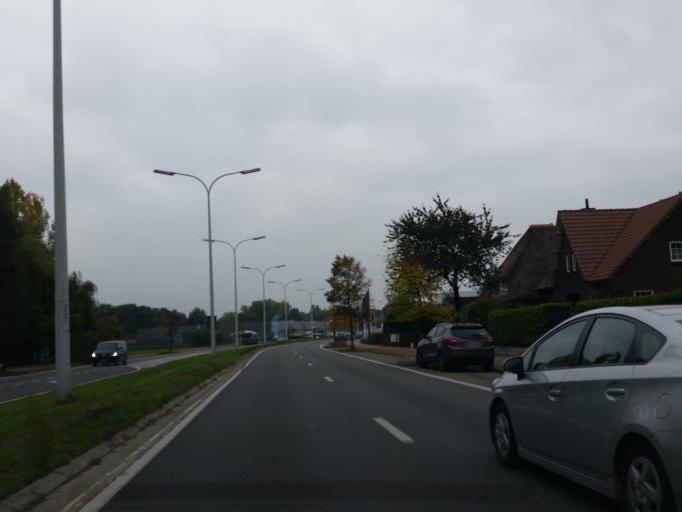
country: BE
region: Flanders
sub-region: Provincie Antwerpen
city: Kontich
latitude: 51.1428
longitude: 4.4579
